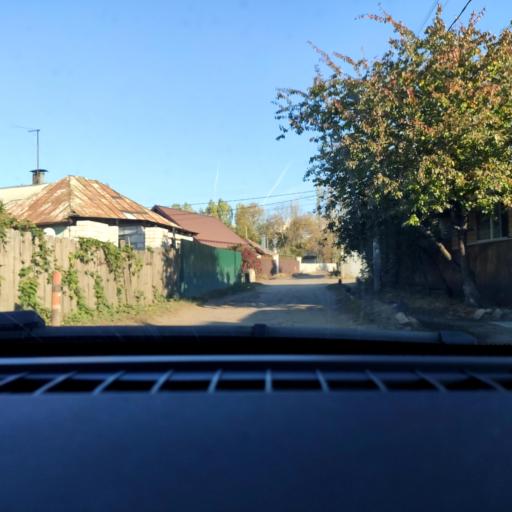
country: RU
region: Voronezj
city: Maslovka
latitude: 51.6312
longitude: 39.2717
